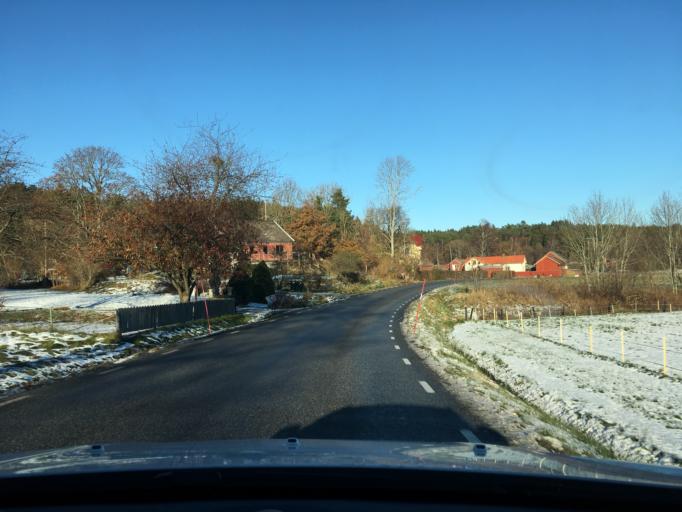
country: SE
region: Vaestra Goetaland
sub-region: Tjorns Kommun
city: Myggenas
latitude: 58.0418
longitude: 11.6734
